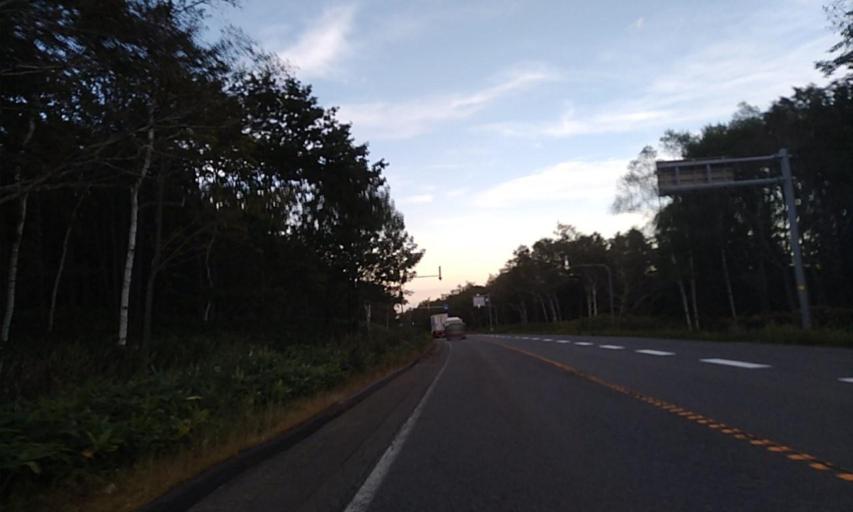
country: JP
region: Hokkaido
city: Otofuke
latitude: 42.9616
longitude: 142.7953
